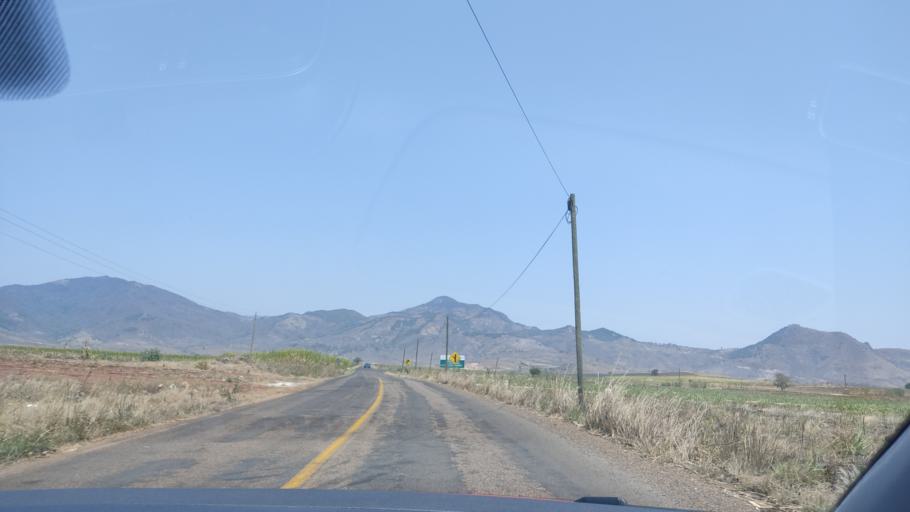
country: MX
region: Nayarit
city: Puga
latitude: 21.5900
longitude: -104.7418
